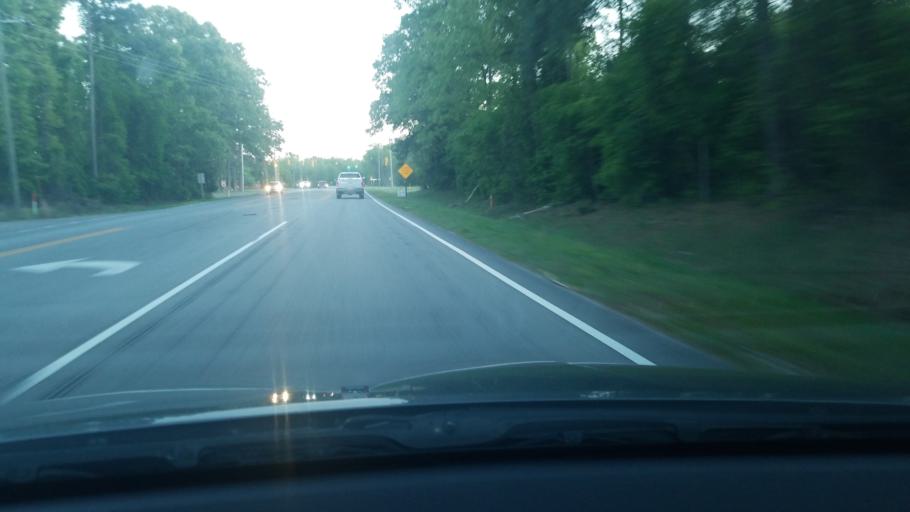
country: US
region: North Carolina
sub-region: Craven County
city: Vanceboro
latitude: 35.2181
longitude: -77.1204
